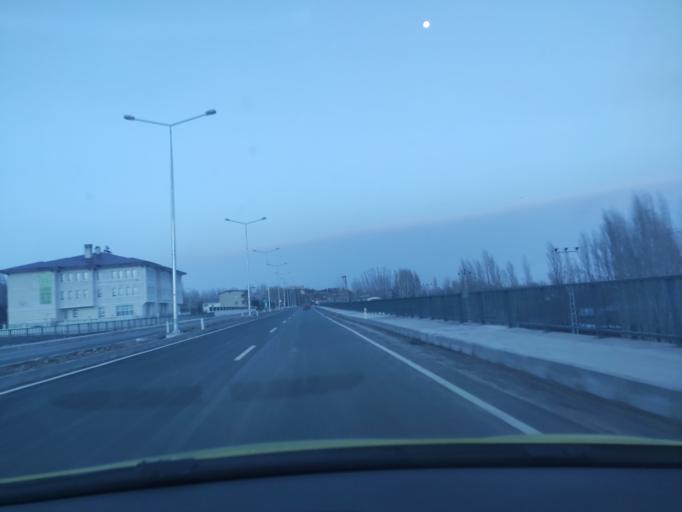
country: TR
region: Bayburt
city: Aydintepe
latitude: 40.3876
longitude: 40.1394
